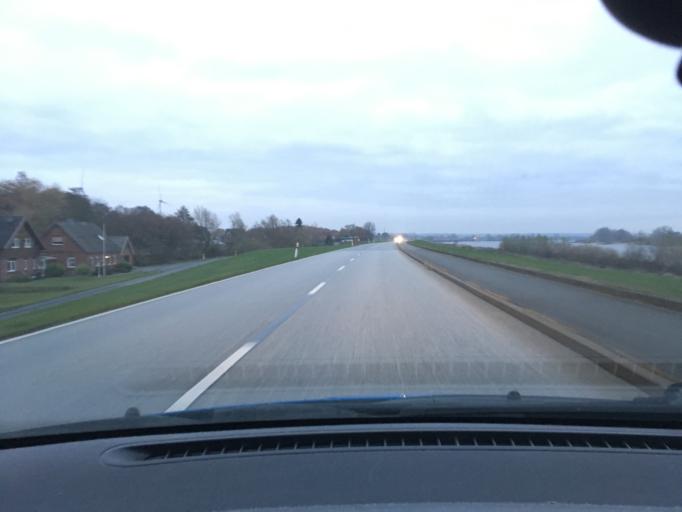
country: DE
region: Lower Saxony
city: Drage
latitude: 53.4054
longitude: 10.2443
